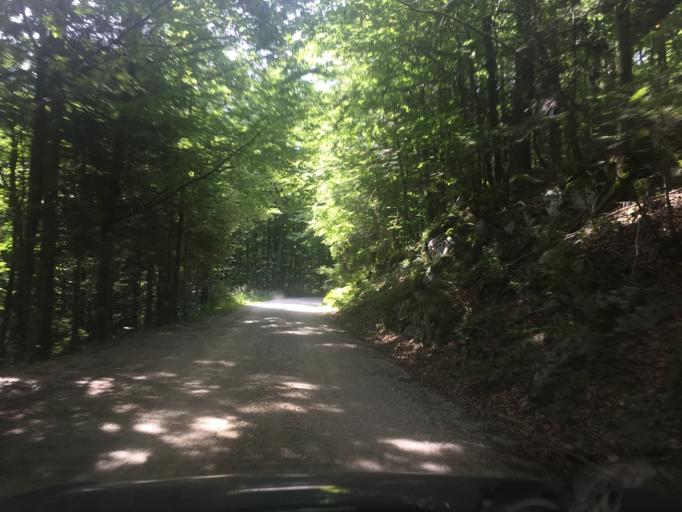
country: SI
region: Ajdovscina
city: Lokavec
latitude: 45.9865
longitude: 13.8386
